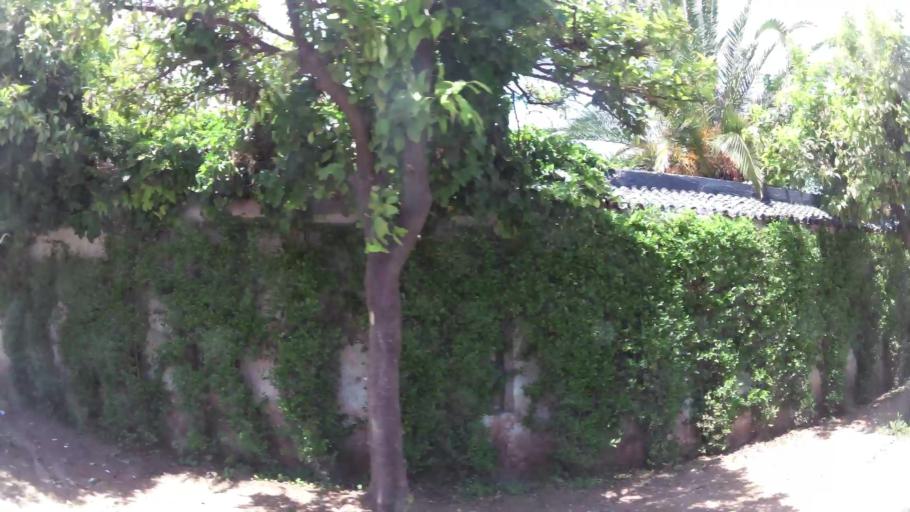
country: MA
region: Fes-Boulemane
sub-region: Fes
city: Fes
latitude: 34.0136
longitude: -4.9953
